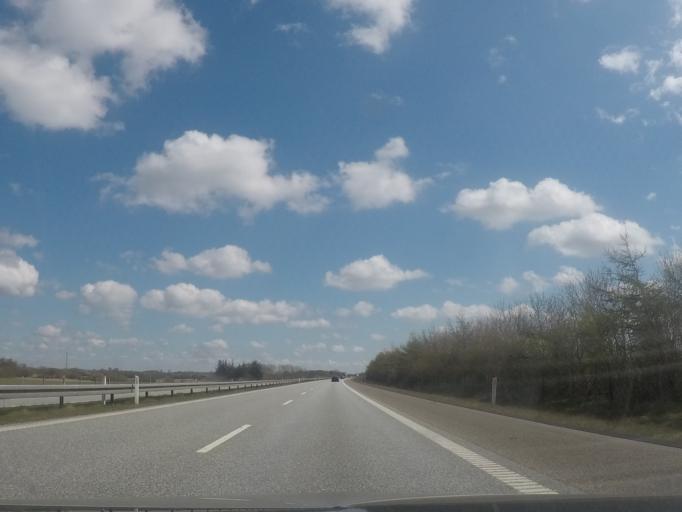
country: DK
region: South Denmark
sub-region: Kolding Kommune
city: Kolding
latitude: 55.5475
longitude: 9.4940
